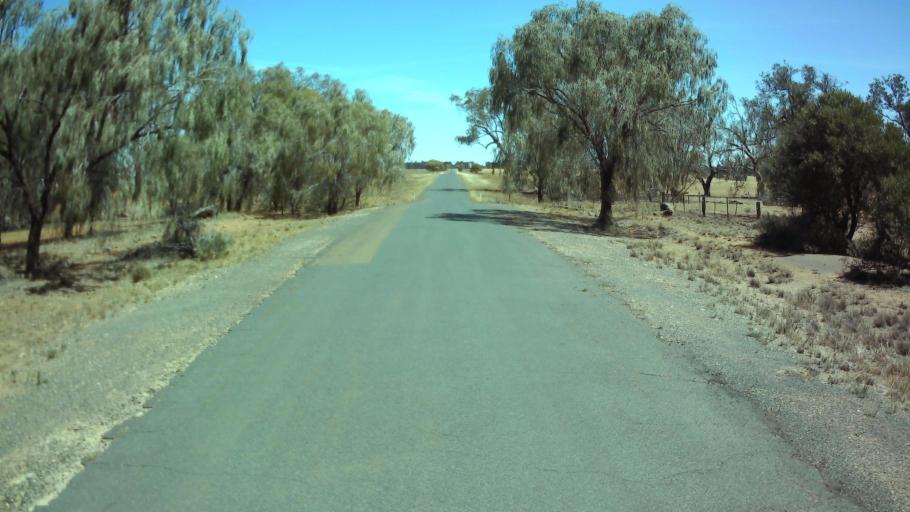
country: AU
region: New South Wales
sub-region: Weddin
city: Grenfell
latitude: -33.8488
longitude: 147.6960
